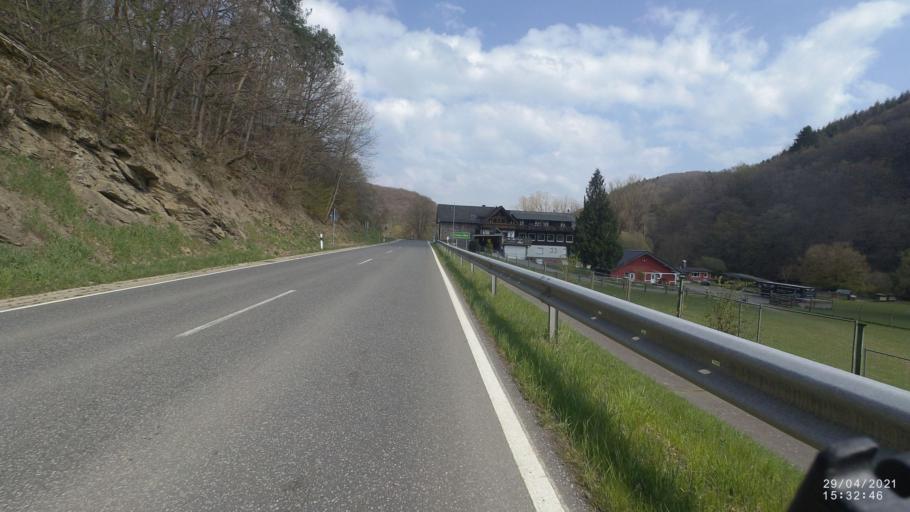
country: DE
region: Rheinland-Pfalz
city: Volkesfeld
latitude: 50.3845
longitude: 7.1470
